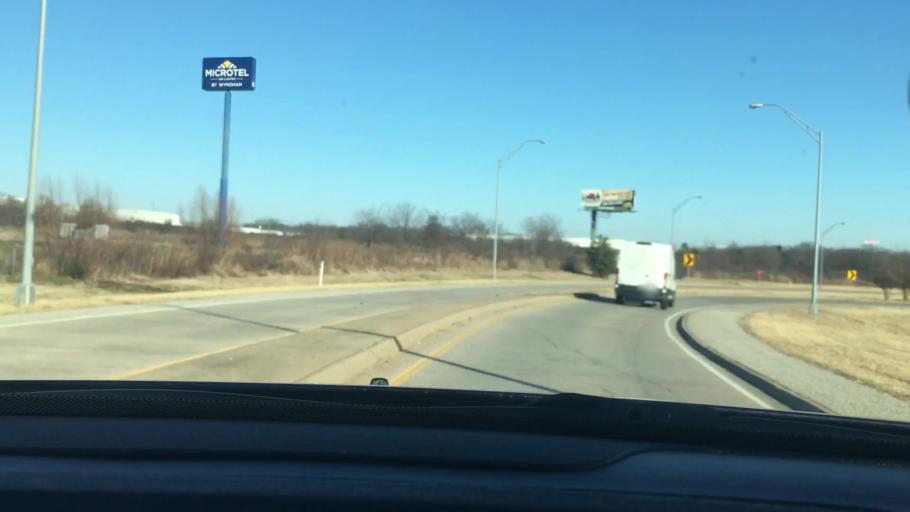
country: US
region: Oklahoma
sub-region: Carter County
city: Ardmore
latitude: 34.1880
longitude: -97.1688
